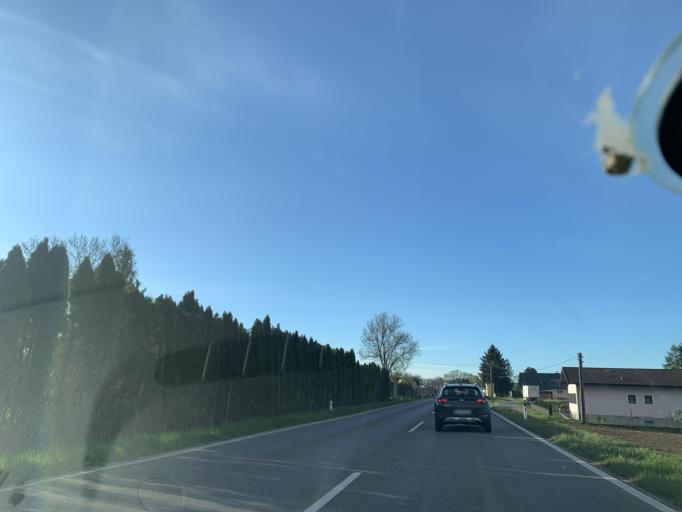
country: AT
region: Styria
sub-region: Politischer Bezirk Leibnitz
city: Kaindorf an der Sulm
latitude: 46.8104
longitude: 15.5280
